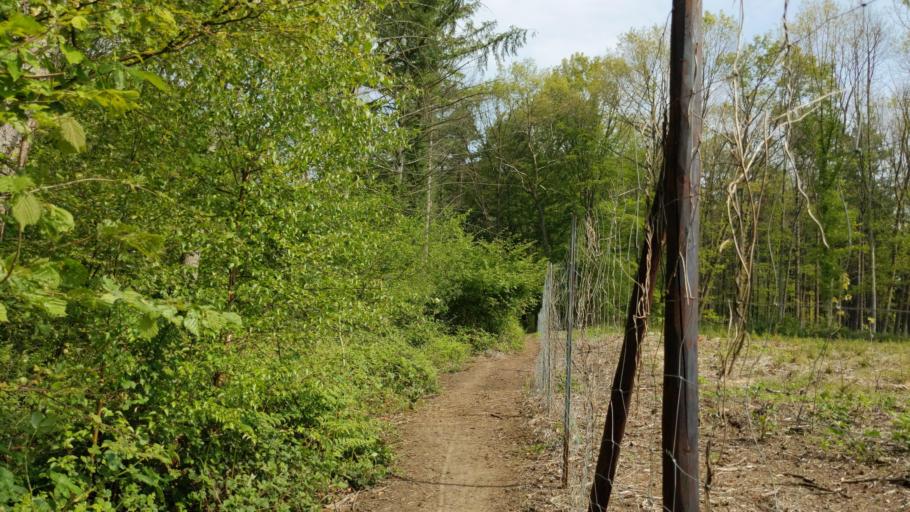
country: DE
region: North Rhine-Westphalia
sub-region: Regierungsbezirk Dusseldorf
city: Meerbusch
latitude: 51.2575
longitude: 6.6505
